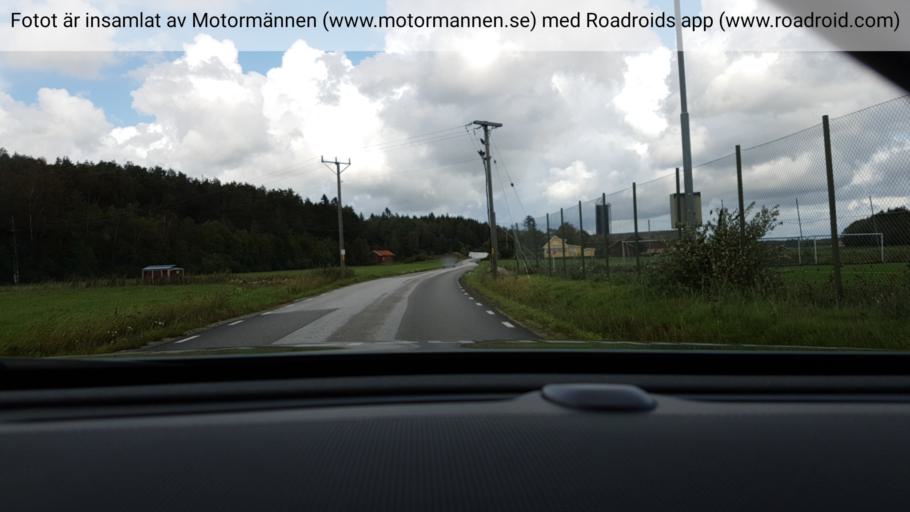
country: SE
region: Vaestra Goetaland
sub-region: Orust
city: Henan
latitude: 58.1435
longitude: 11.5726
